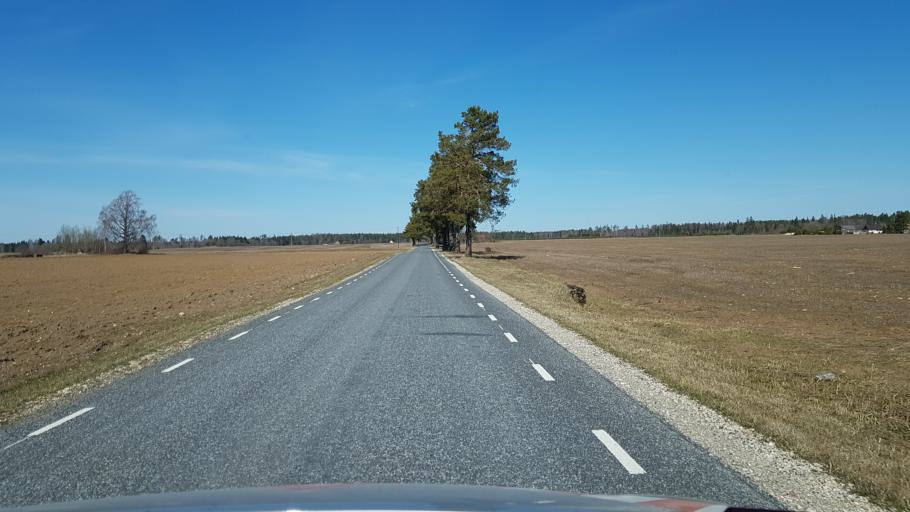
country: EE
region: Laeaene-Virumaa
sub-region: Vinni vald
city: Vinni
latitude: 59.1089
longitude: 26.5248
